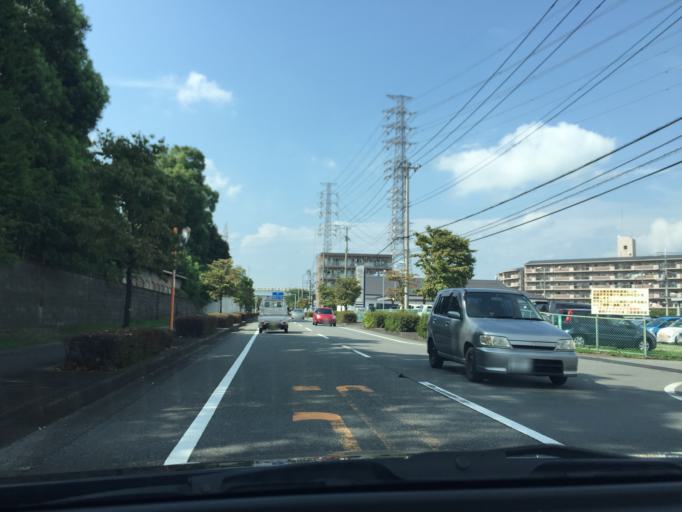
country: JP
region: Shizuoka
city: Mishima
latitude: 35.1464
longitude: 138.9052
